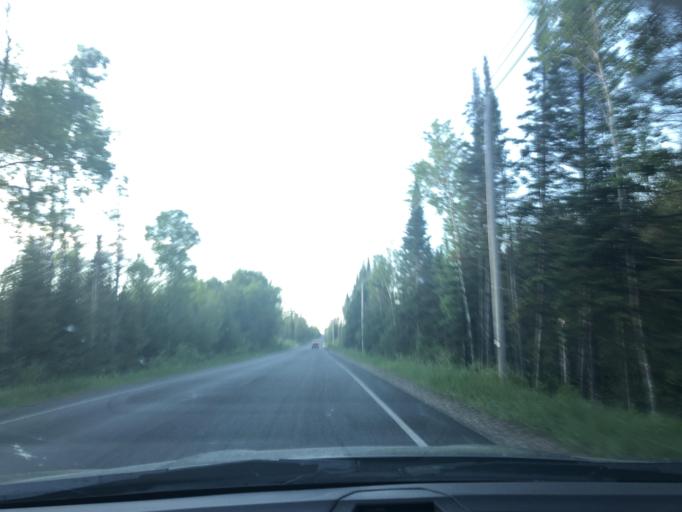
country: US
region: Michigan
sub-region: Missaukee County
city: Lake City
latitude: 44.3635
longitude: -85.0760
